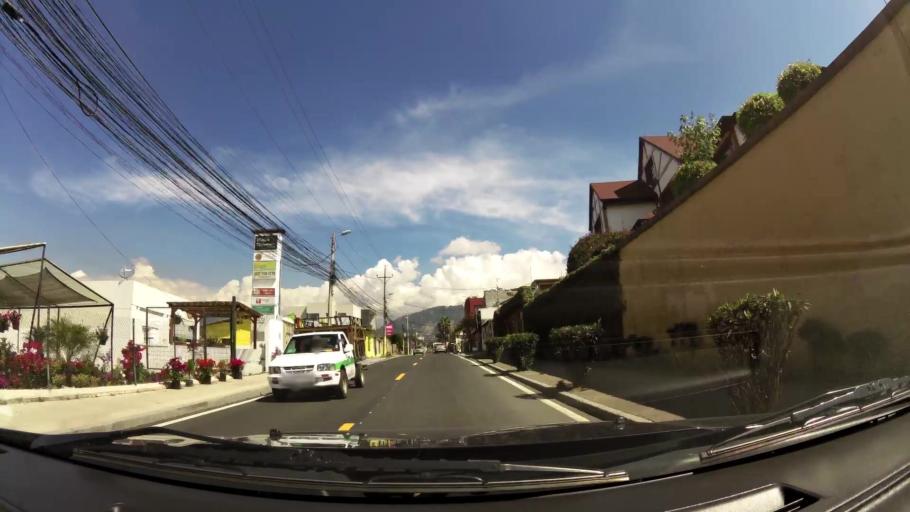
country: EC
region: Pichincha
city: Quito
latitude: -0.2025
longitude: -78.4246
